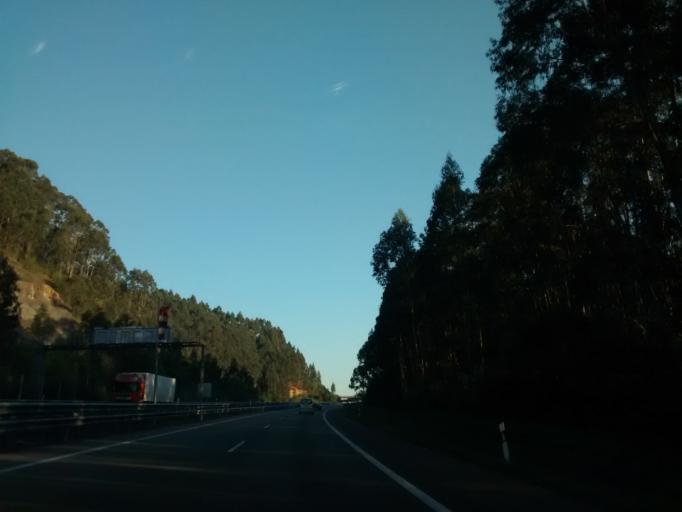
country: ES
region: Asturias
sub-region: Province of Asturias
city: Arriba
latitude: 43.5013
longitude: -5.5407
